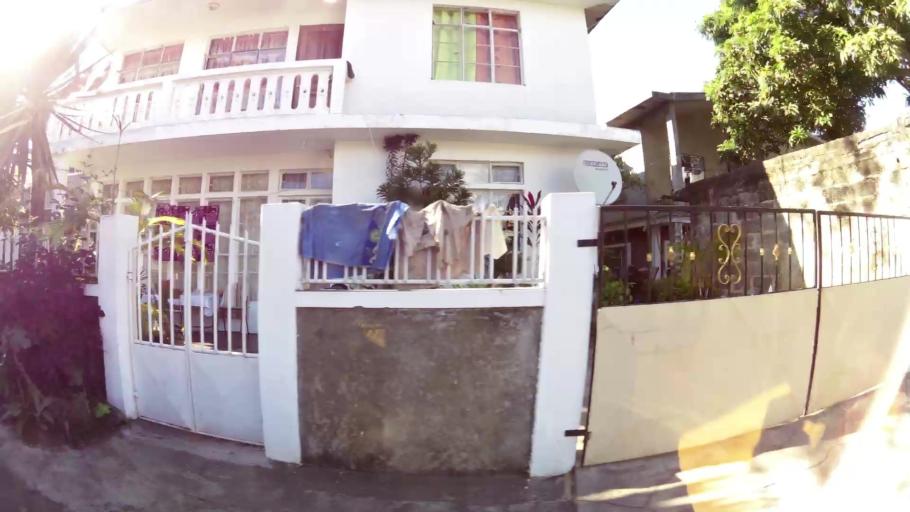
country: MU
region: Grand Port
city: Mahebourg
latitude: -20.4134
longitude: 57.7089
